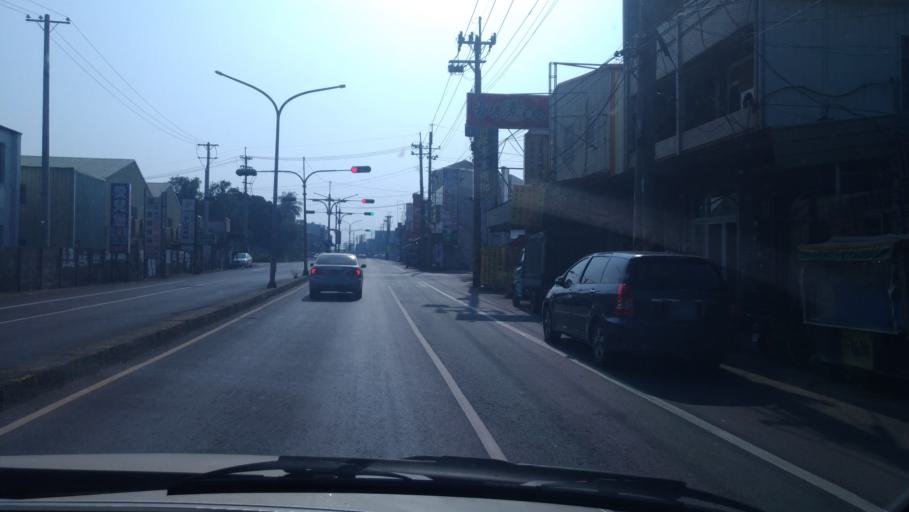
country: TW
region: Taiwan
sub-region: Chiayi
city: Jiayi Shi
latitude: 23.5180
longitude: 120.4274
